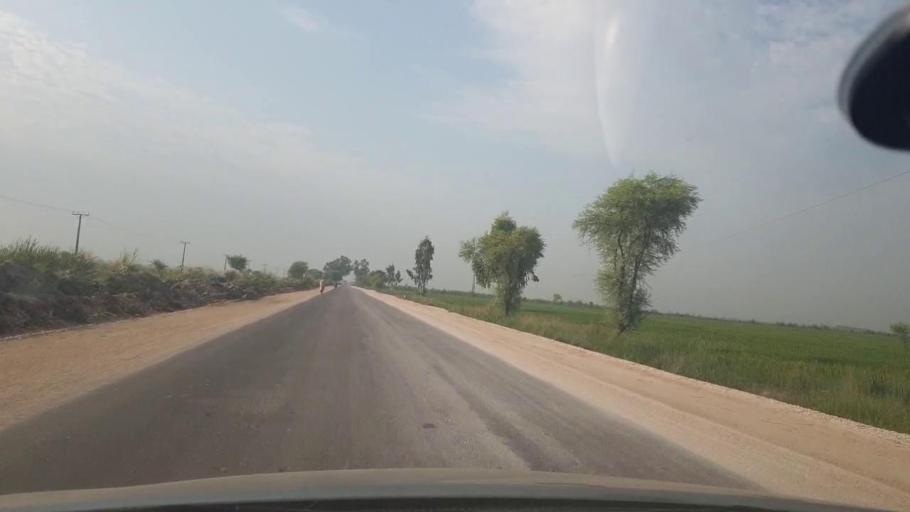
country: PK
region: Sindh
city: Jacobabad
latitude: 28.1881
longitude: 68.3675
